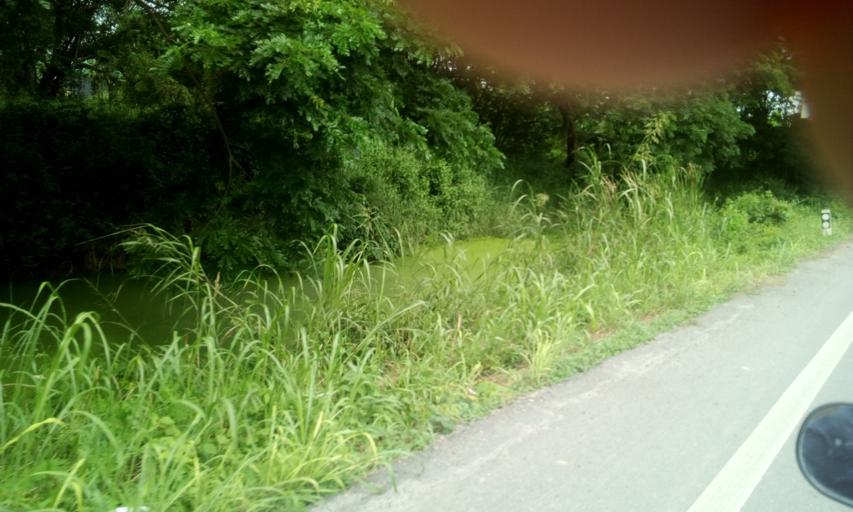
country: TH
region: Pathum Thani
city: Ban Lam Luk Ka
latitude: 13.9975
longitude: 100.8421
